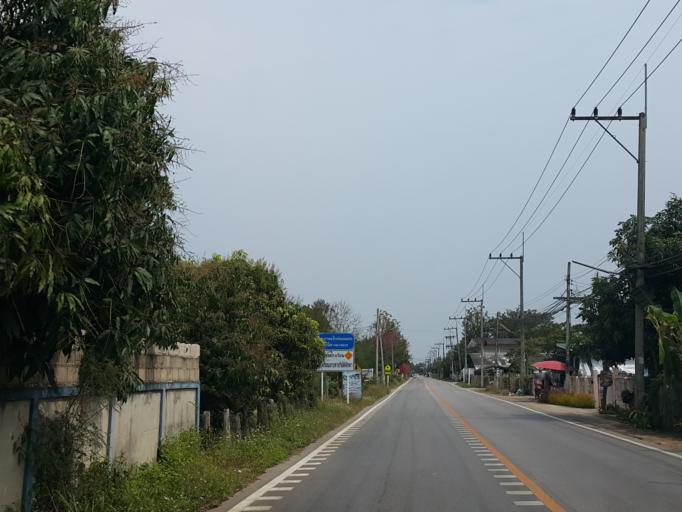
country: TH
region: Lampang
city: Ko Kha
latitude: 18.1714
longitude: 99.3885
